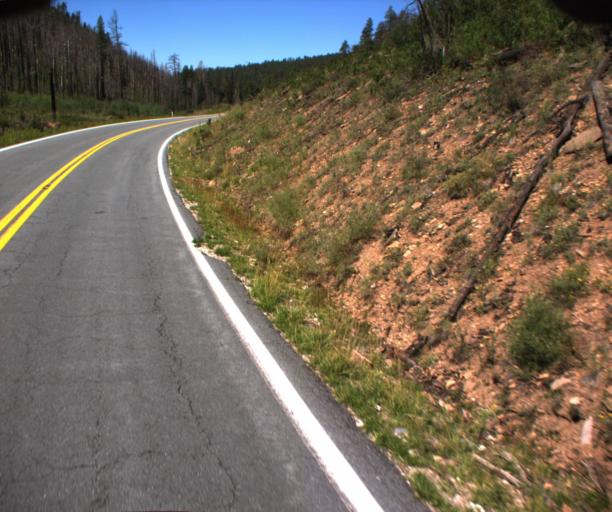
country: US
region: Arizona
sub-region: Apache County
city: Eagar
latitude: 33.7930
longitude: -109.1566
